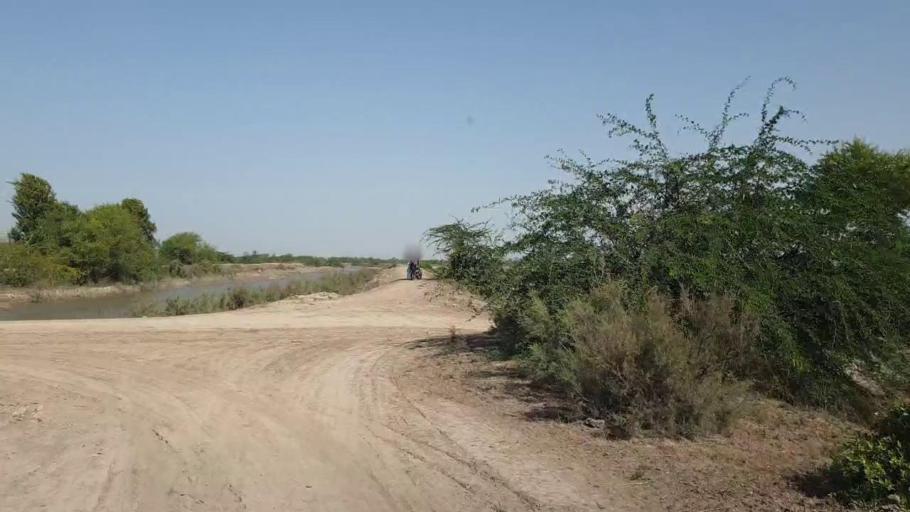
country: PK
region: Sindh
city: Tando Bago
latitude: 24.6687
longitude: 69.0682
